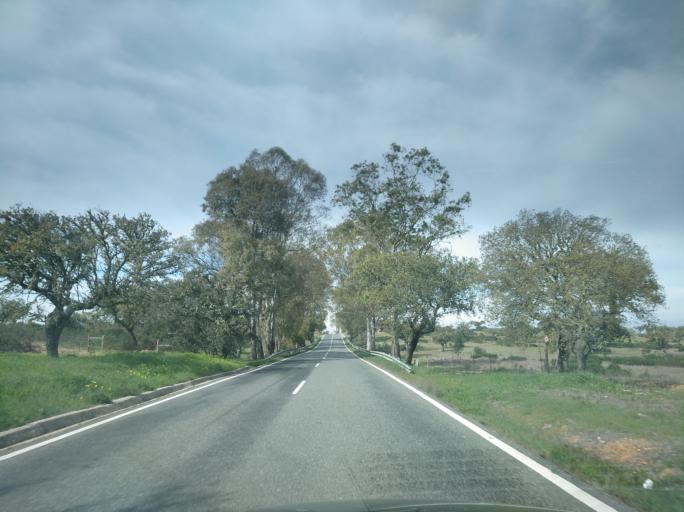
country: PT
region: Beja
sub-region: Mertola
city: Mertola
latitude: 37.7343
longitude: -7.7715
